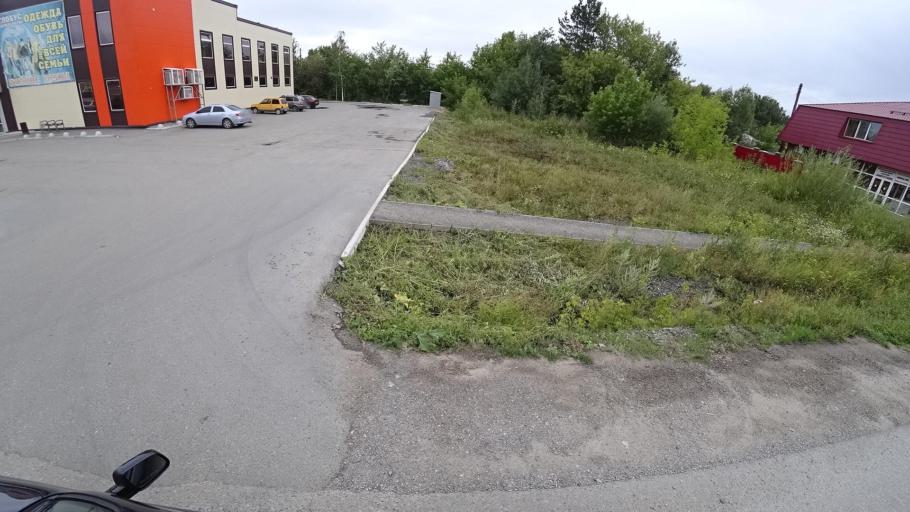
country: RU
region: Sverdlovsk
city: Kamyshlov
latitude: 56.8382
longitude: 62.7328
